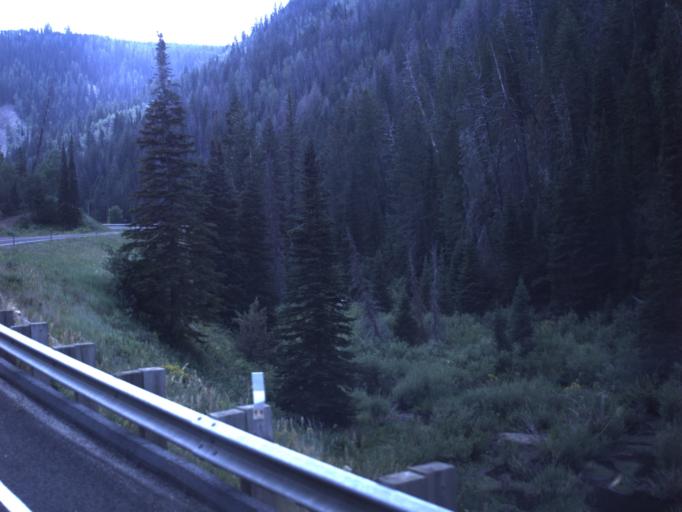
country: US
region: Utah
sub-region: Summit County
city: Francis
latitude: 40.5286
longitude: -111.0942
